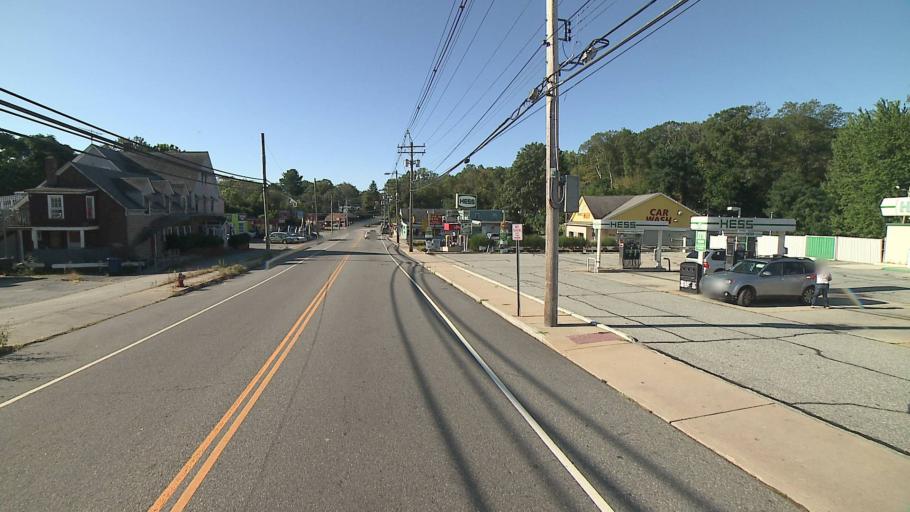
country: US
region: Connecticut
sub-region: New London County
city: Norwich
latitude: 41.5454
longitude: -72.0545
